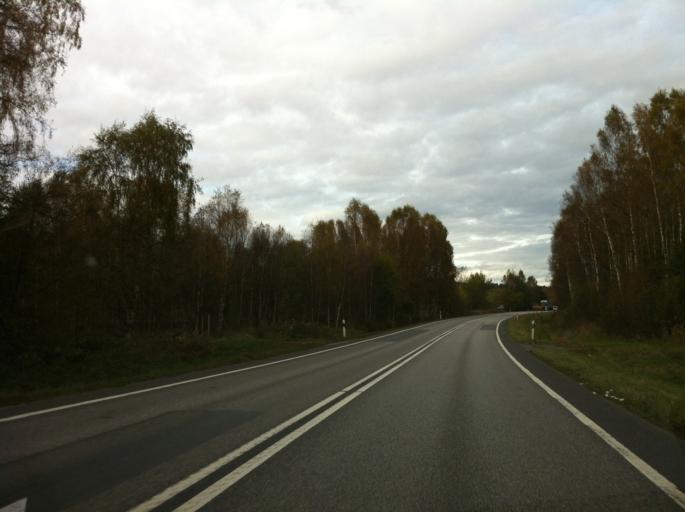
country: SE
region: OEstergoetland
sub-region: Motala Kommun
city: Ryd
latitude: 58.6676
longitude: 14.9680
